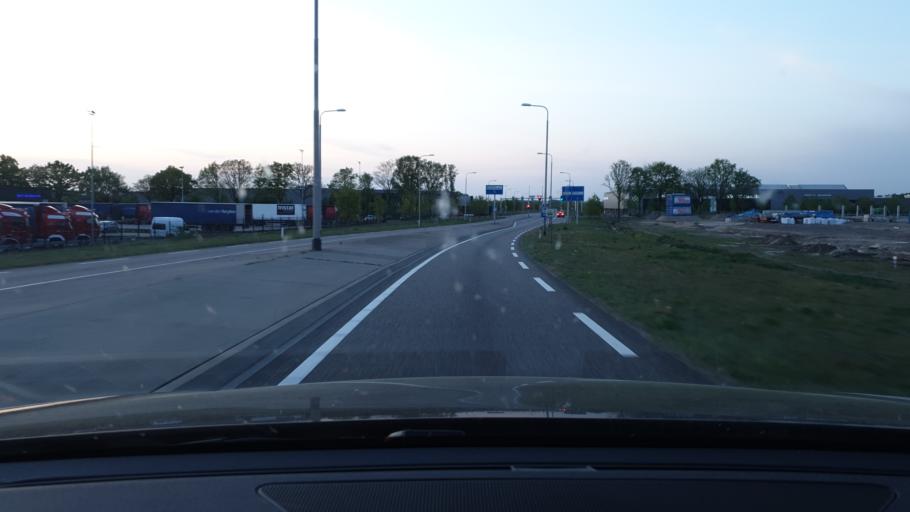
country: NL
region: North Brabant
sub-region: Gemeente Eersel
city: Eersel
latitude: 51.3532
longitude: 5.2730
